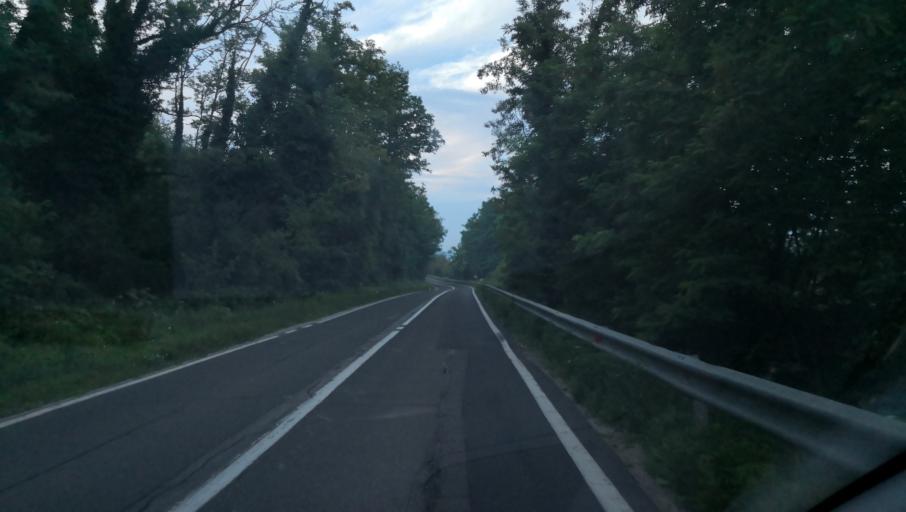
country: SI
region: Metlika
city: Metlika
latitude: 45.6567
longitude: 15.2947
